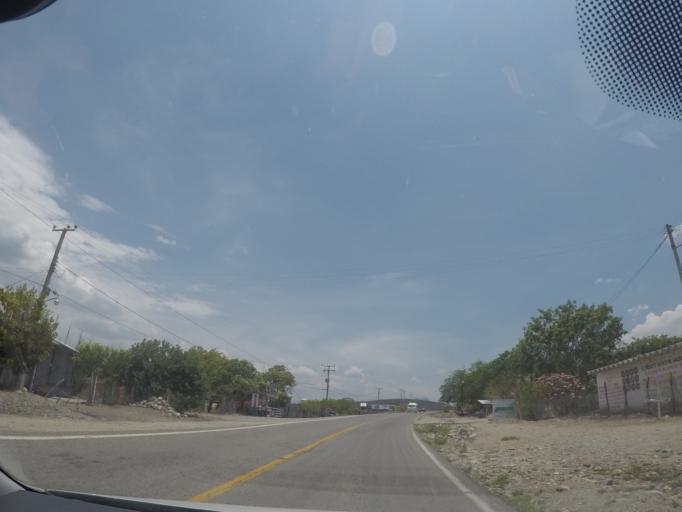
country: MX
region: Oaxaca
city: Magdalena Tequisistlan
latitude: 16.4155
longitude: -95.5986
